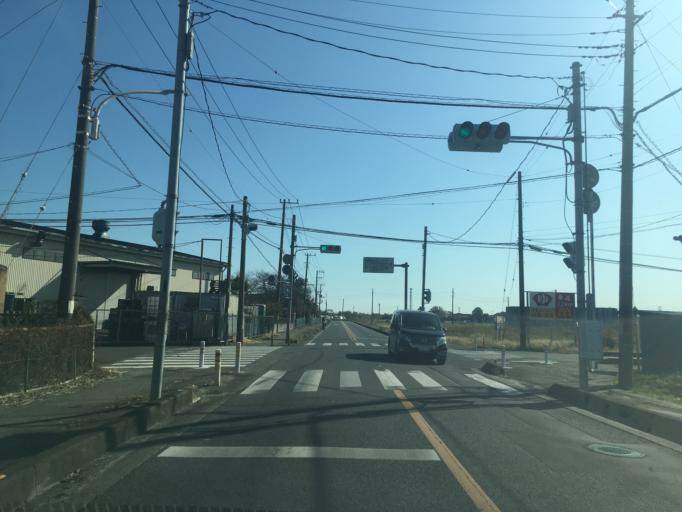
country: JP
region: Saitama
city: Kawagoe
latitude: 35.9448
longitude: 139.4624
